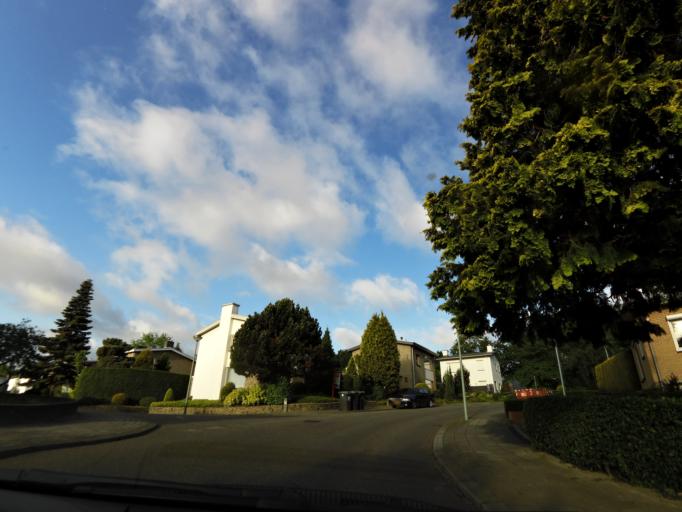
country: NL
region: Limburg
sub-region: Gemeente Brunssum
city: Brunssum
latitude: 50.9398
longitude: 5.9668
